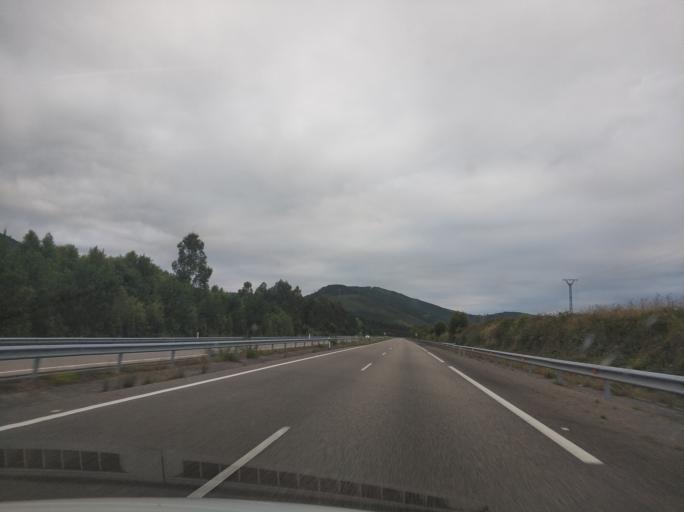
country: ES
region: Asturias
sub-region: Province of Asturias
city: Tineo
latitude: 43.5442
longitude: -6.4721
